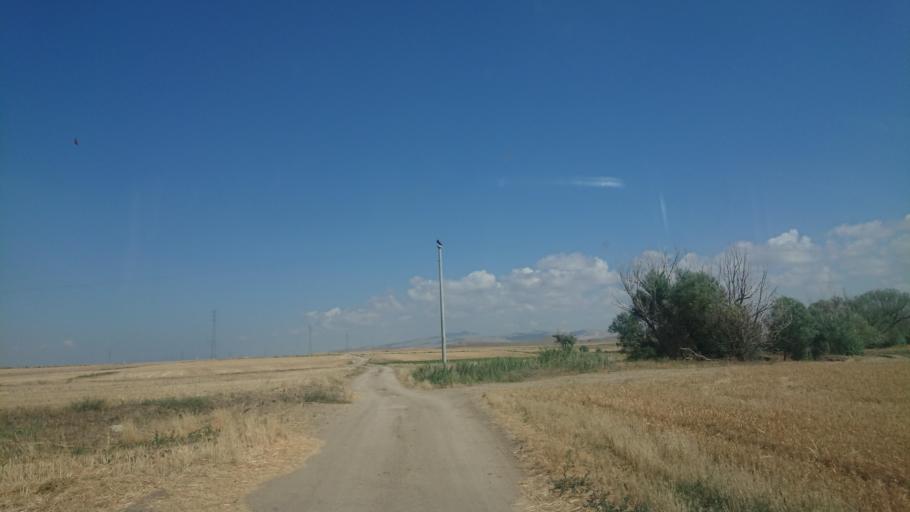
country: TR
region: Aksaray
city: Sariyahsi
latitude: 38.9974
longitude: 33.8939
